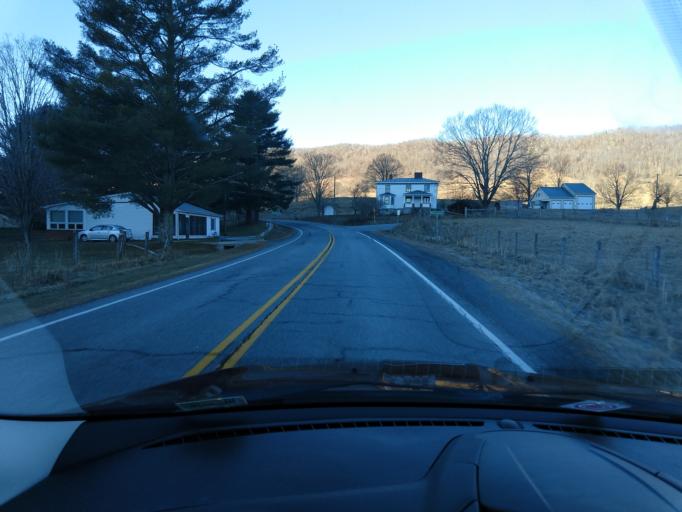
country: US
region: Virginia
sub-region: Highland County
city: Monterey
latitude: 38.3760
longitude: -79.6644
